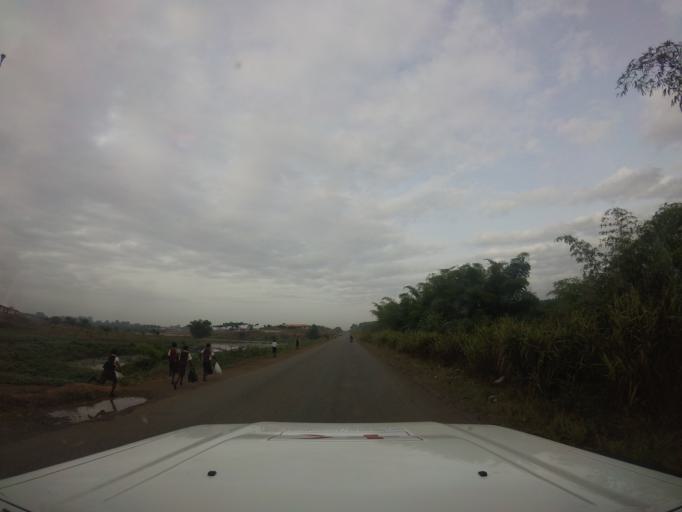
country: LR
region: Bomi
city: Tubmanburg
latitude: 6.7303
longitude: -11.0118
